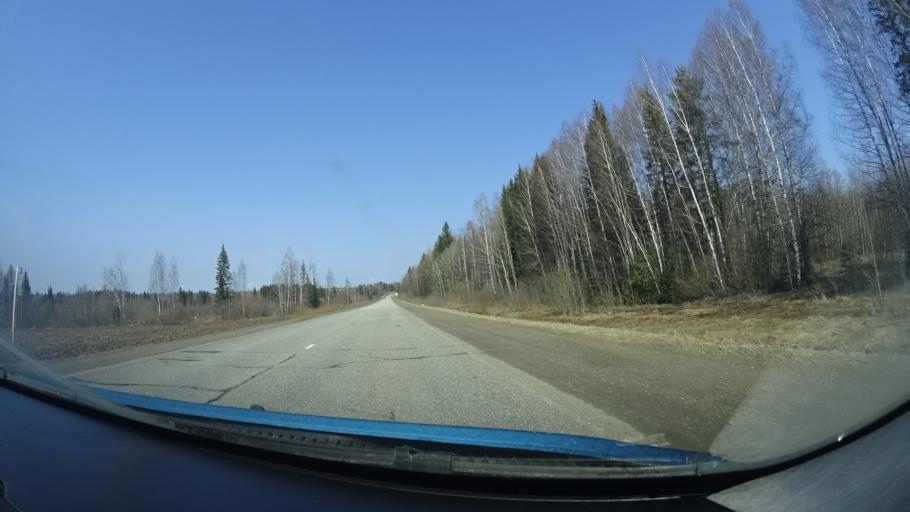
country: RU
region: Perm
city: Osa
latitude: 57.3821
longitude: 55.6091
